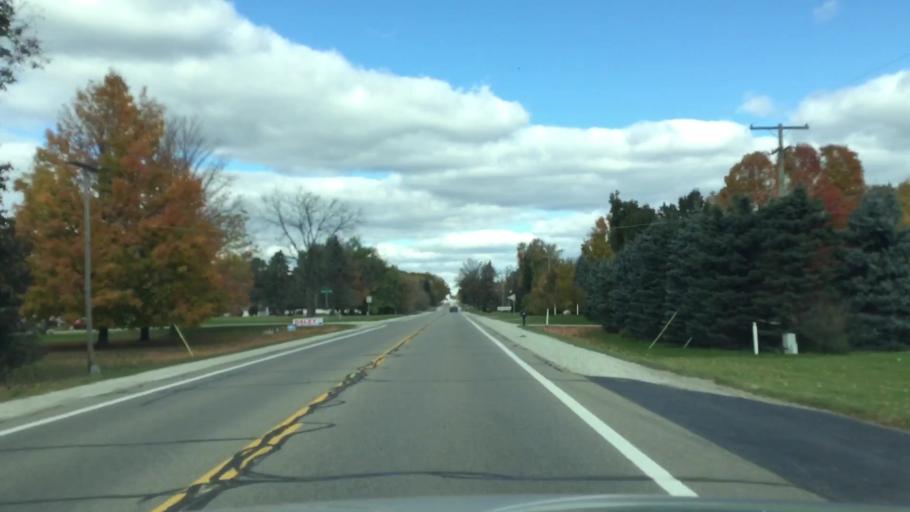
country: US
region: Michigan
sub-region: Lapeer County
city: Lapeer
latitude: 43.1018
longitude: -83.3083
